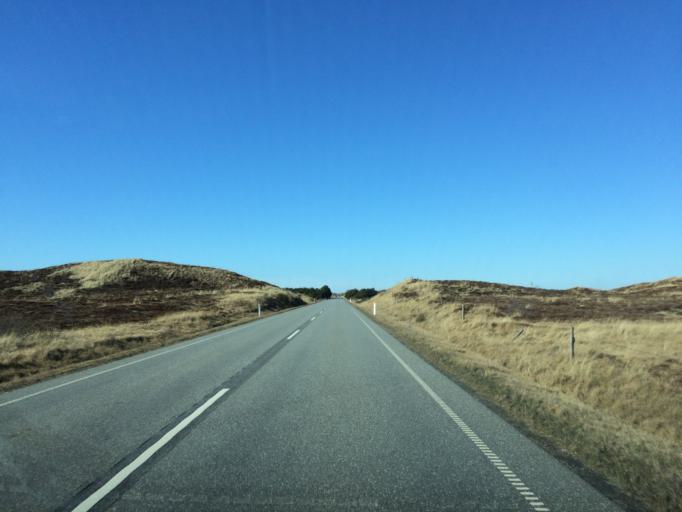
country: DK
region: Central Jutland
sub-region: Ringkobing-Skjern Kommune
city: Hvide Sande
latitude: 55.8946
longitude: 8.1708
